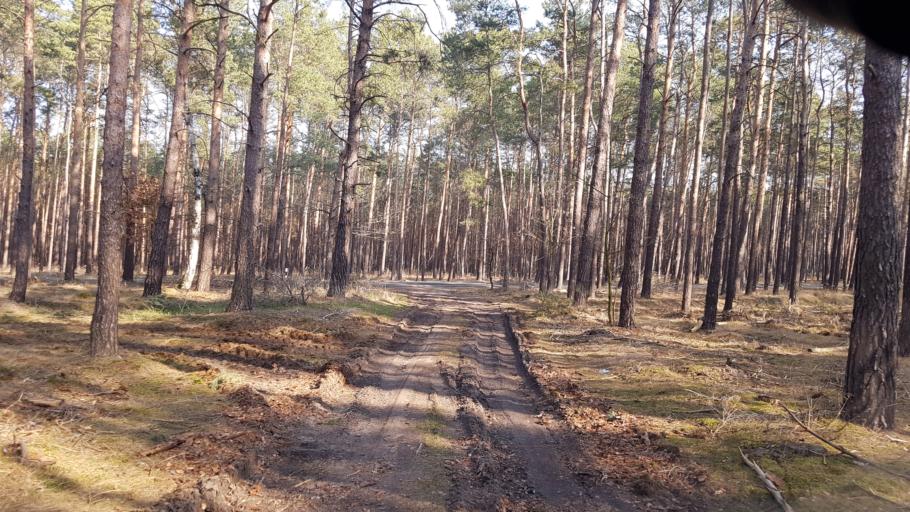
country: DE
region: Brandenburg
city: Schlieben
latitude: 51.6779
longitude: 13.3219
